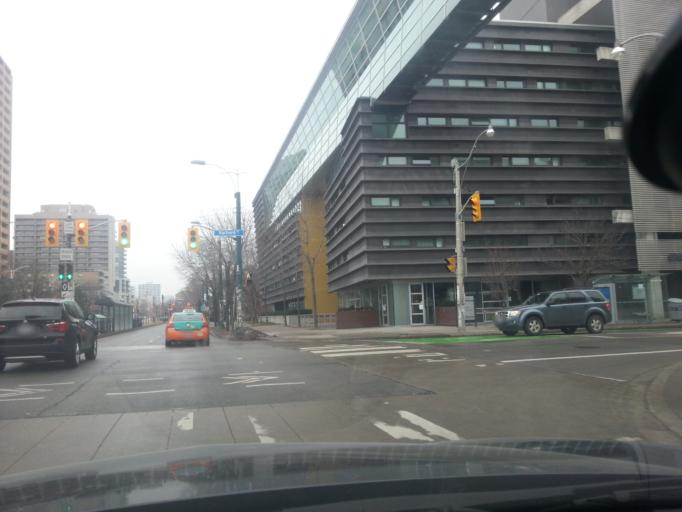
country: CA
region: Ontario
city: Toronto
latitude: 43.6630
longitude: -79.4019
